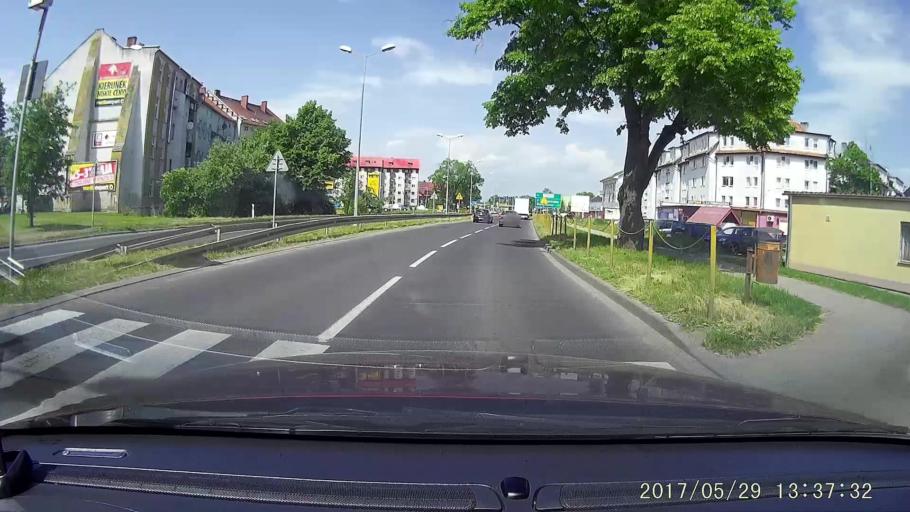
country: PL
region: Lower Silesian Voivodeship
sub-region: Powiat lubanski
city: Luban
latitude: 51.1162
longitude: 15.2935
